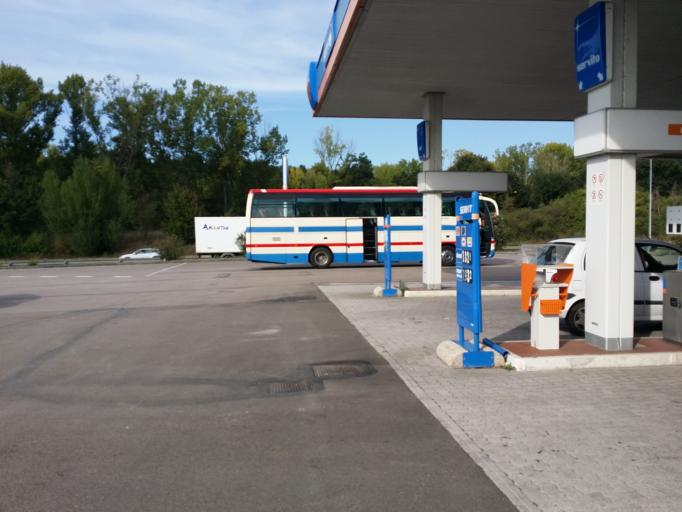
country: IT
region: Umbria
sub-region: Provincia di Perugia
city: Umbertide
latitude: 43.3164
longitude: 12.3334
